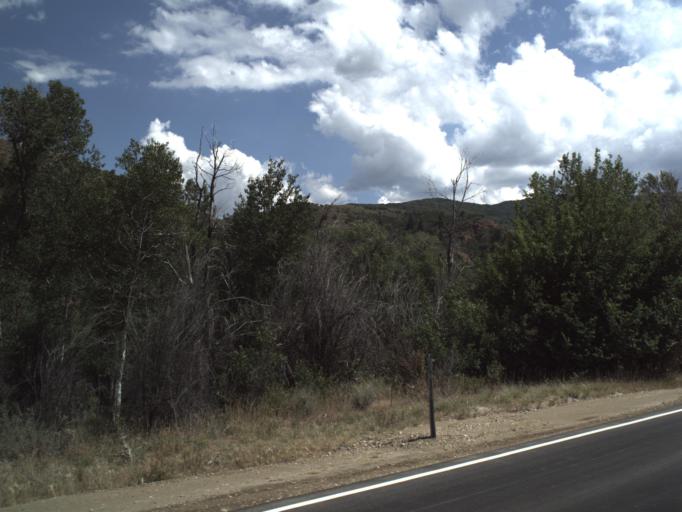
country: US
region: Utah
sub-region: Weber County
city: Wolf Creek
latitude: 41.3029
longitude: -111.6183
